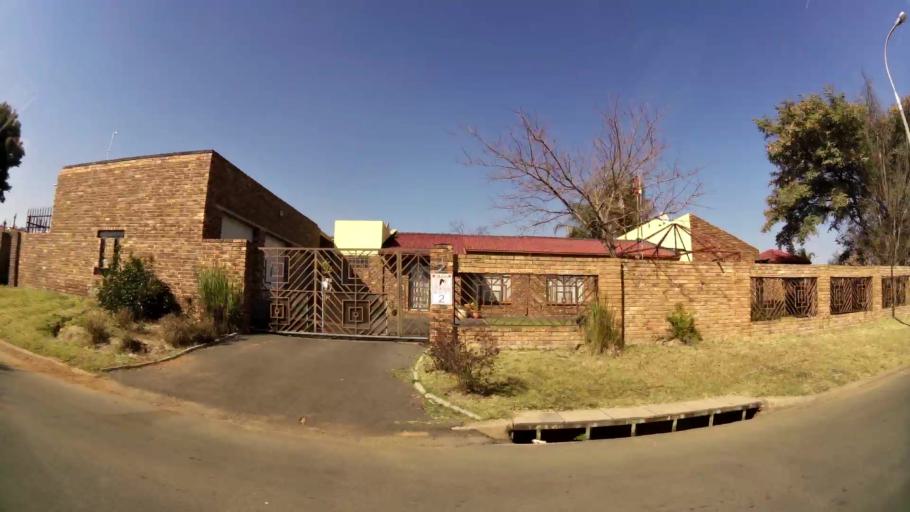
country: ZA
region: Gauteng
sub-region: Ekurhuleni Metropolitan Municipality
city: Tembisa
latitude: -26.0458
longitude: 28.2264
